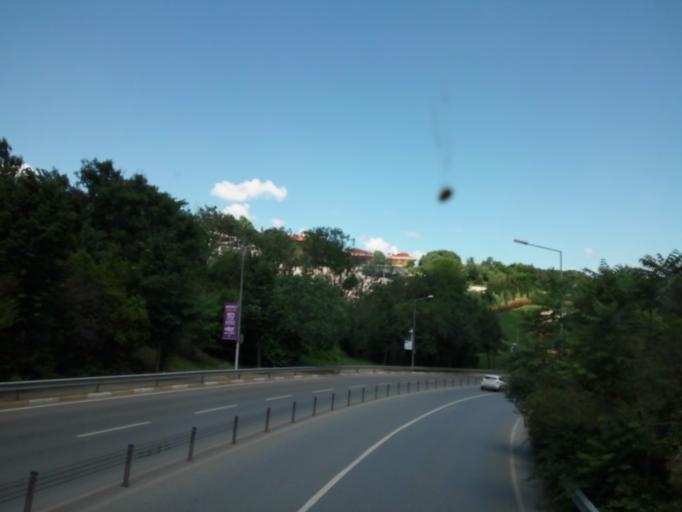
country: TR
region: Istanbul
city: UEskuedar
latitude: 41.0333
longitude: 29.0422
